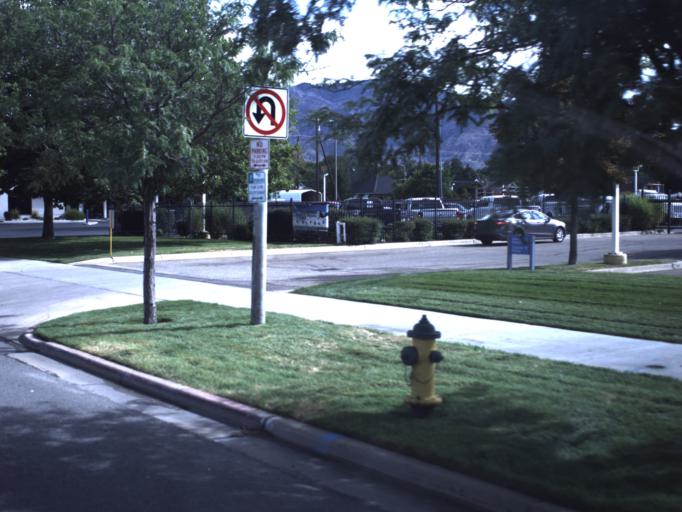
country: US
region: Utah
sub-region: Weber County
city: Ogden
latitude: 41.2111
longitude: -111.9706
